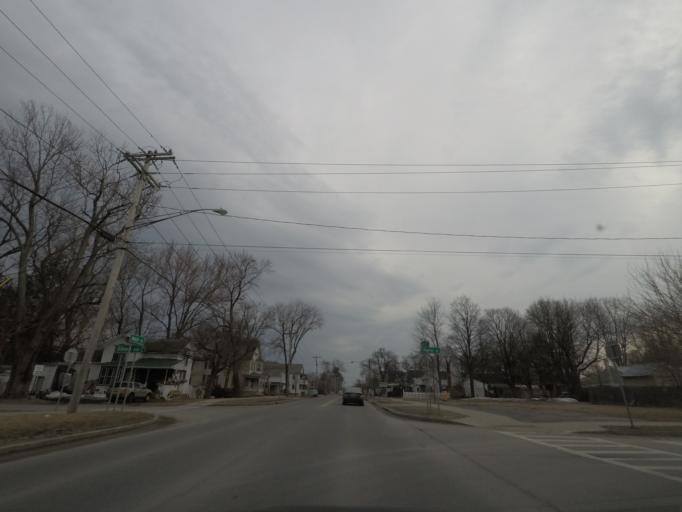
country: US
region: New York
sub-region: Washington County
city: Hudson Falls
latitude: 43.2914
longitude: -73.5867
